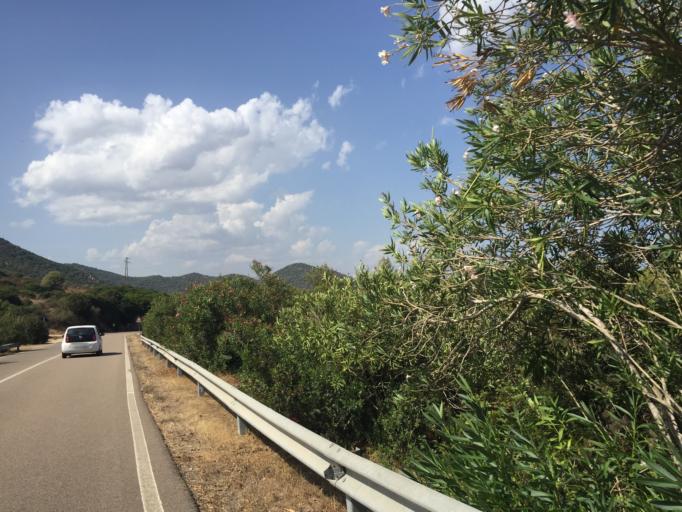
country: IT
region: Sardinia
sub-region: Provincia di Cagliari
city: Villasimius
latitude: 39.1701
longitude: 9.5581
